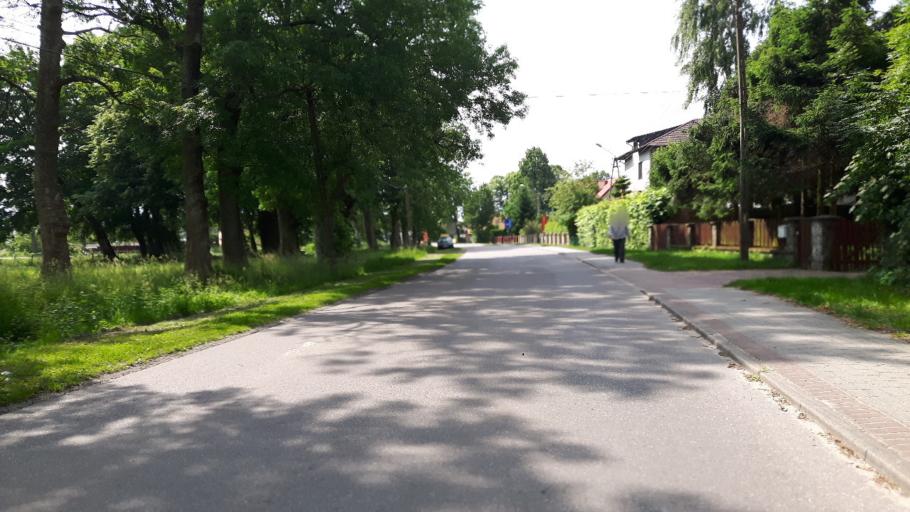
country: PL
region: Pomeranian Voivodeship
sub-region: Powiat leborski
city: Leba
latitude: 54.7520
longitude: 17.5880
